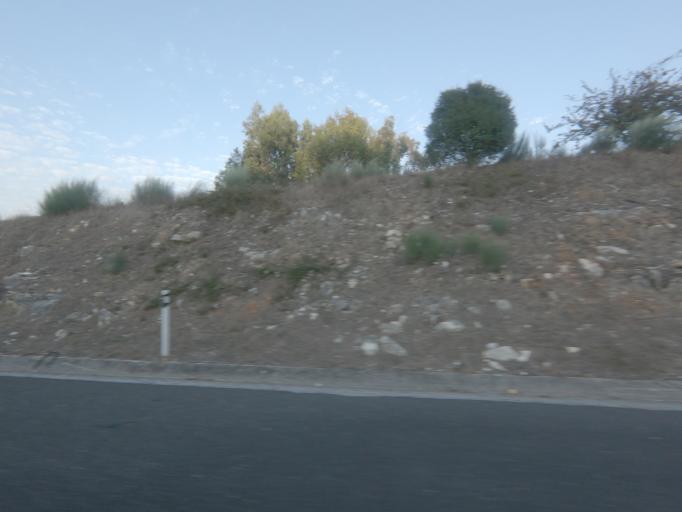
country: PT
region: Leiria
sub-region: Leiria
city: Santa Catarina da Serra
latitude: 39.6772
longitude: -8.6837
